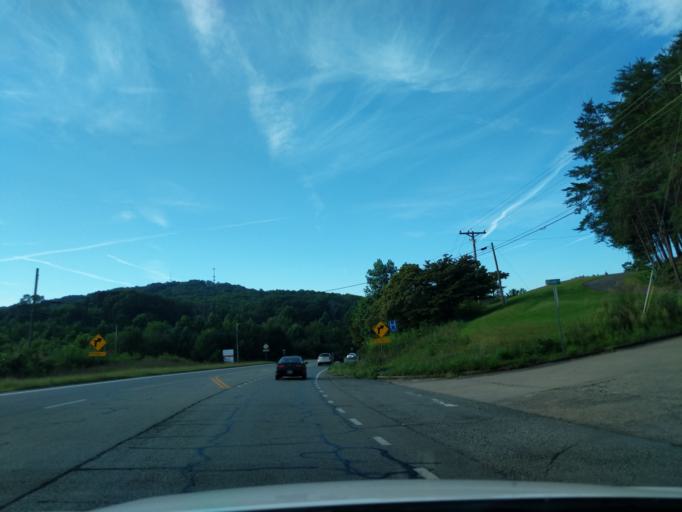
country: US
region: Georgia
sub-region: Fannin County
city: McCaysville
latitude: 34.9156
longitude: -84.3763
